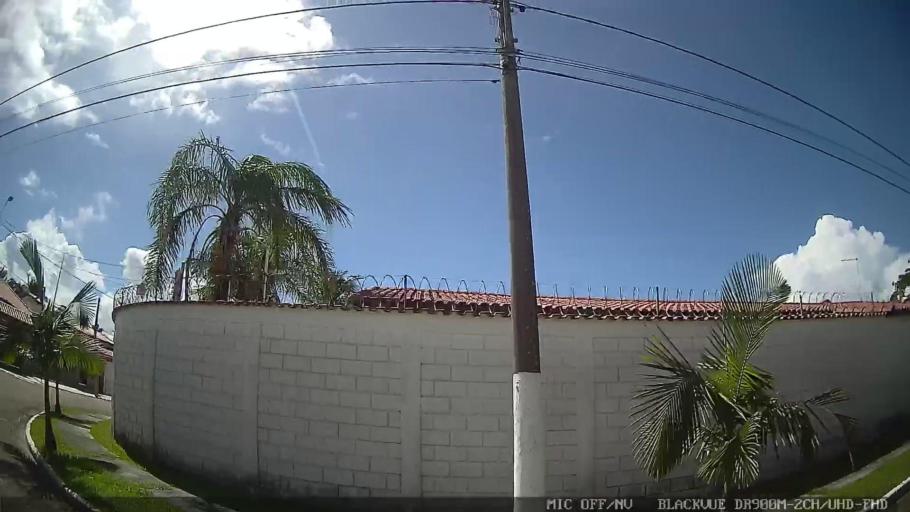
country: BR
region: Sao Paulo
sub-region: Itanhaem
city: Itanhaem
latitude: -24.2326
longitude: -46.8725
